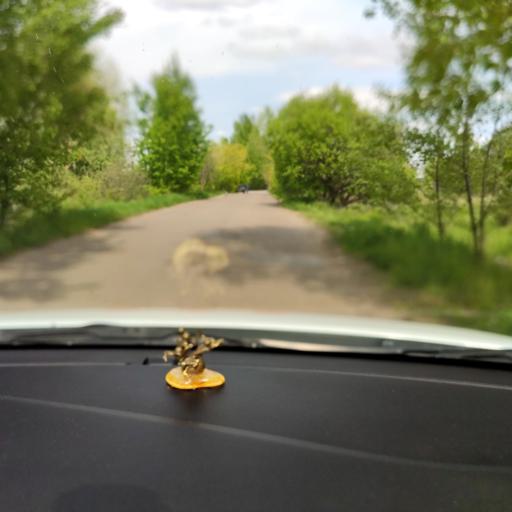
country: RU
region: Tatarstan
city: Verkhniy Uslon
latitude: 55.6995
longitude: 49.0625
